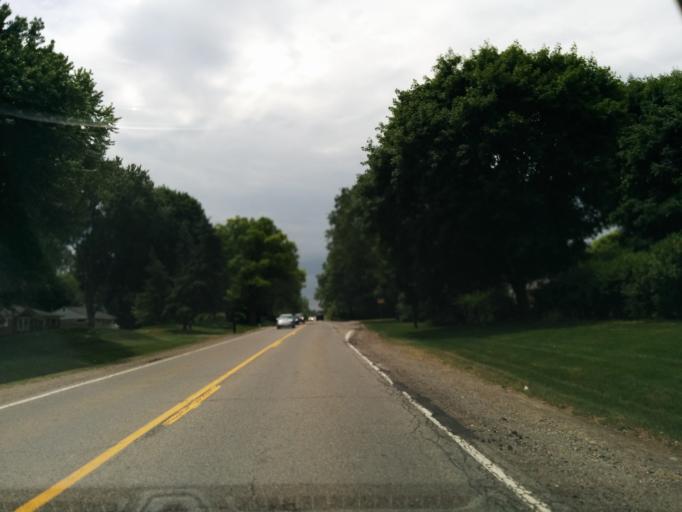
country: US
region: Michigan
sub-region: Oakland County
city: Wolverine Lake
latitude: 42.5490
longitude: -83.4585
